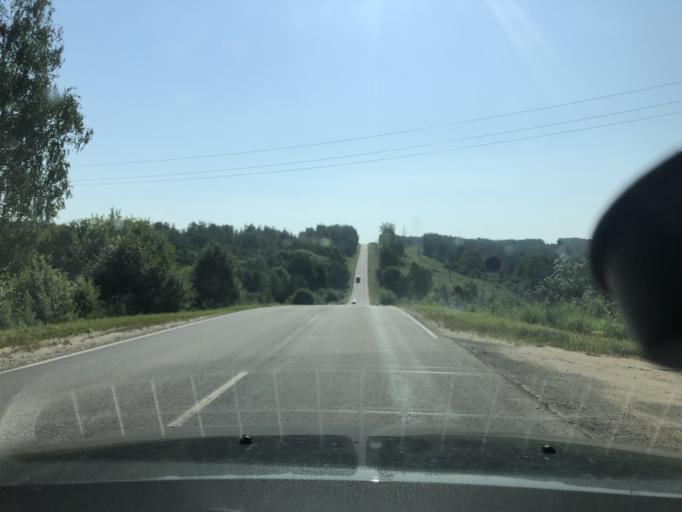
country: RU
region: Tula
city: Dubna
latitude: 54.1456
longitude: 36.9845
